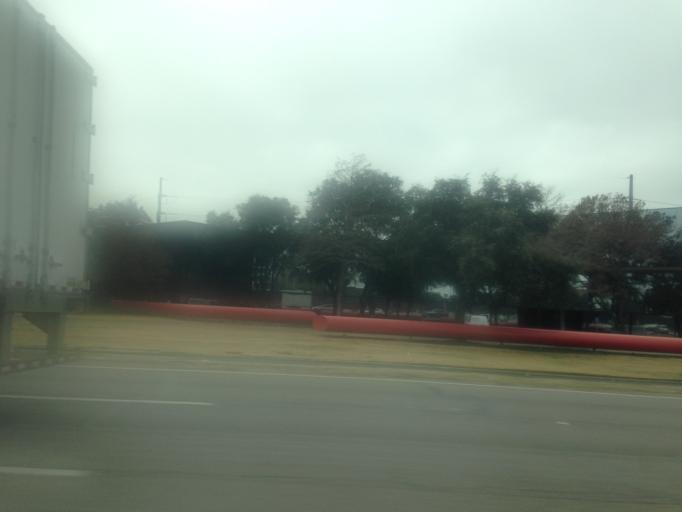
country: US
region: Texas
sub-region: Dallas County
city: Dallas
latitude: 32.8093
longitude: -96.8462
